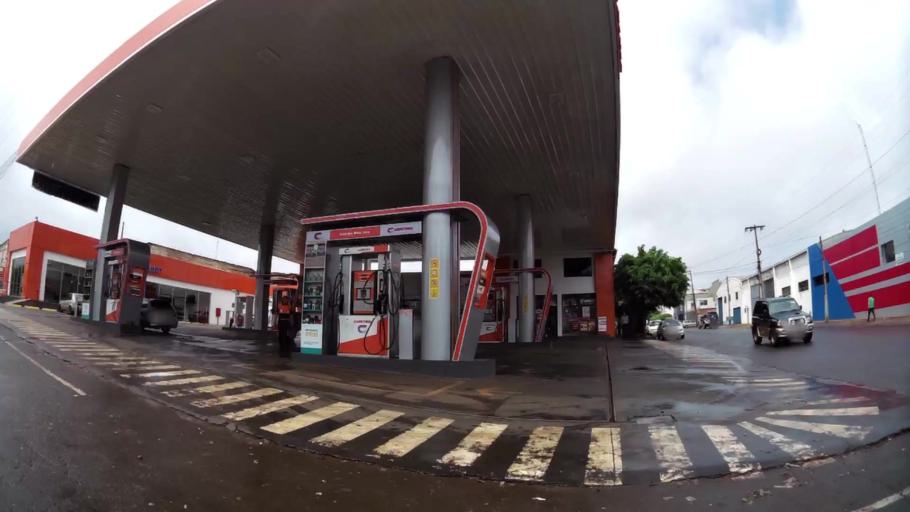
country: PY
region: Alto Parana
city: Ciudad del Este
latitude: -25.5012
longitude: -54.6577
